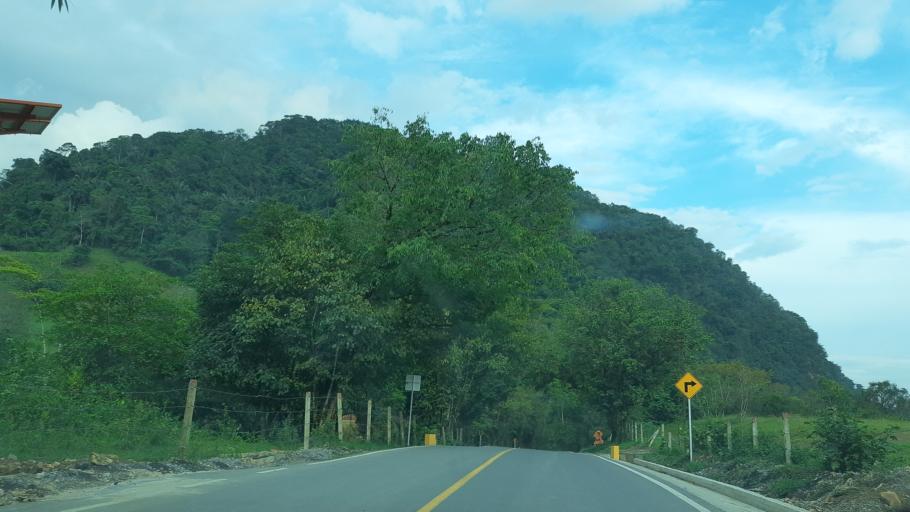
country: CO
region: Boyaca
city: Santa Maria
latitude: 4.8559
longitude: -73.2331
